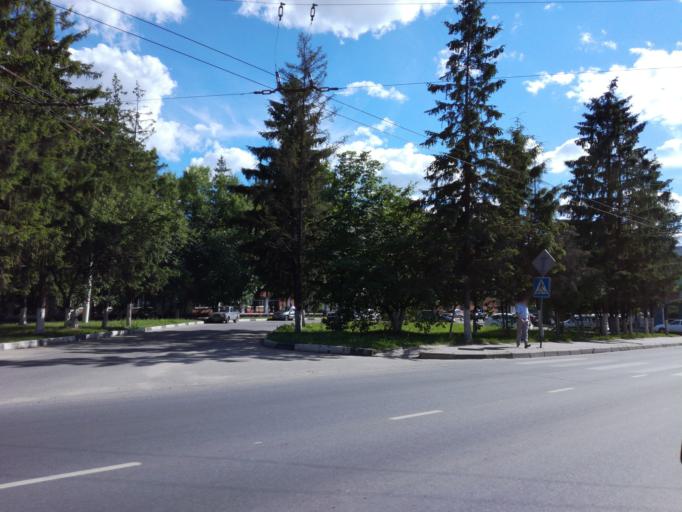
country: RU
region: Kursk
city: Kursk
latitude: 51.7642
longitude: 36.1760
